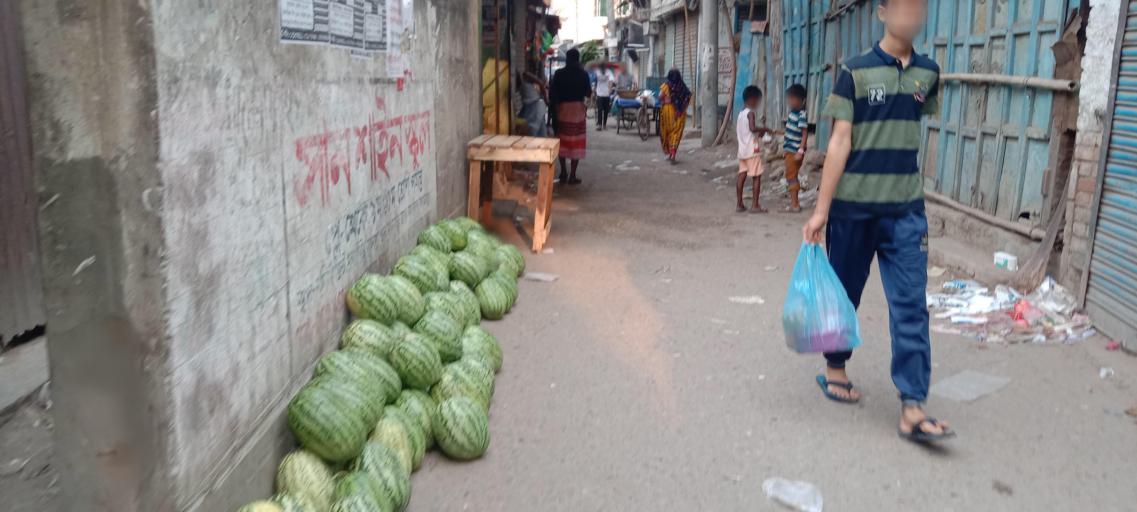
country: BD
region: Dhaka
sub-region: Dhaka
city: Dhaka
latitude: 23.7050
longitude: 90.3835
